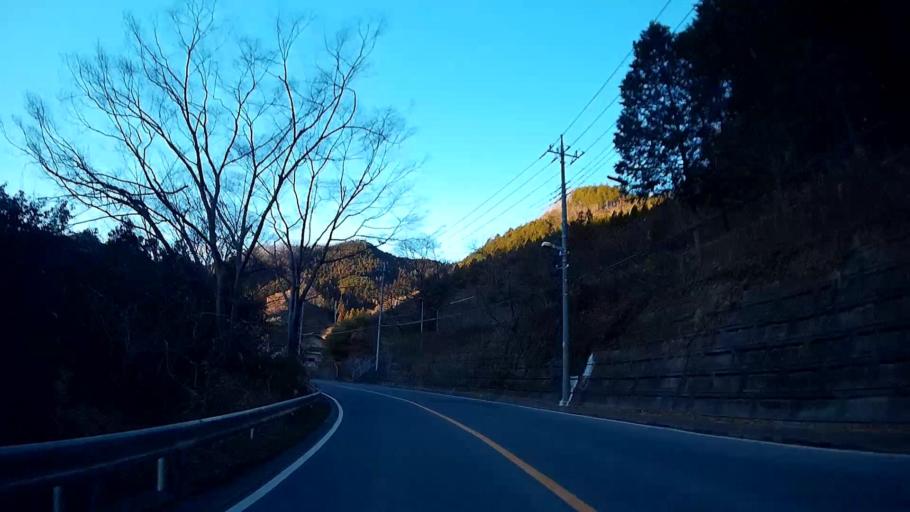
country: JP
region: Saitama
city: Chichibu
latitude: 36.0481
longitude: 139.0133
